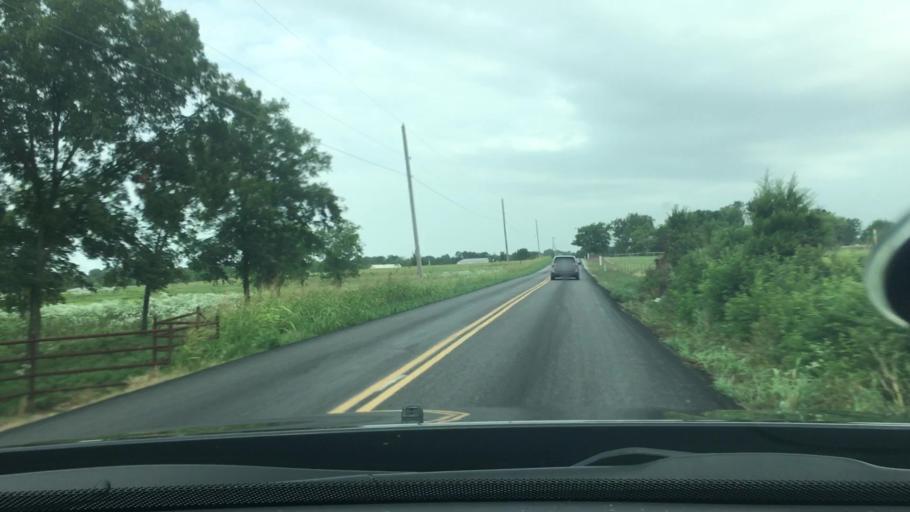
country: US
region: Oklahoma
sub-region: Carter County
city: Ardmore
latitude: 34.2020
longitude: -97.1994
